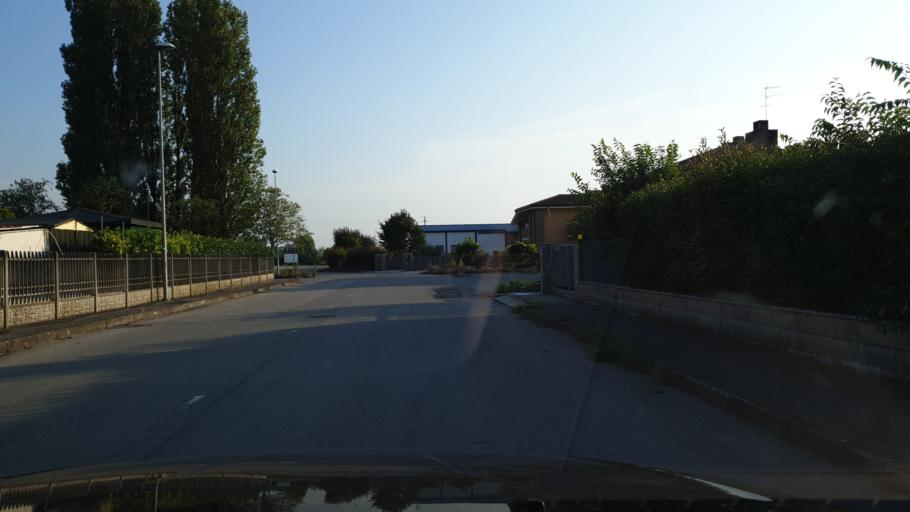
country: IT
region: Veneto
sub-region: Provincia di Rovigo
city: Fratta Polesine
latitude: 45.0257
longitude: 11.6367
